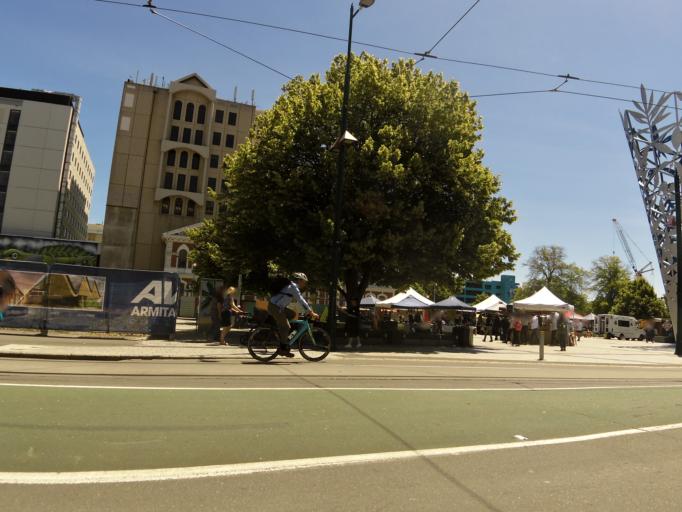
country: NZ
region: Canterbury
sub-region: Christchurch City
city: Christchurch
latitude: -43.5317
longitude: 172.6367
